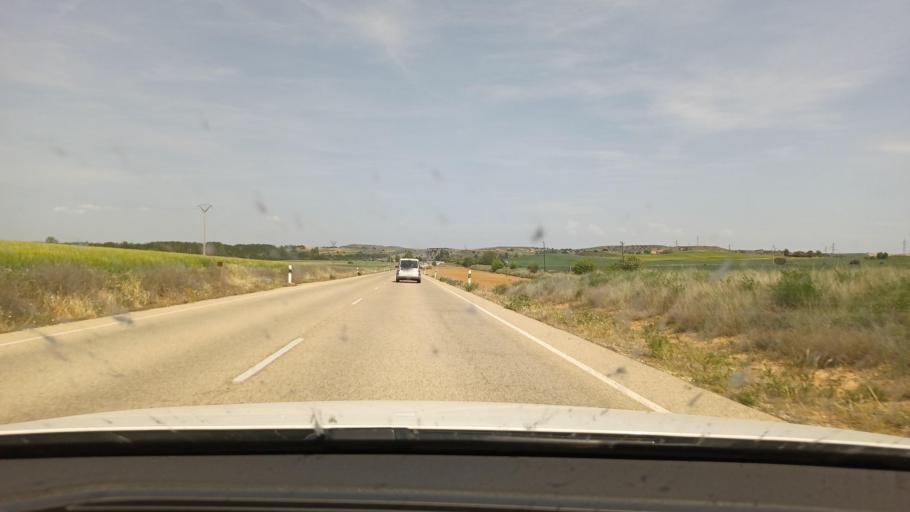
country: ES
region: Castille and Leon
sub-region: Provincia de Soria
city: Barca
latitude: 41.4652
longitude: -2.6278
